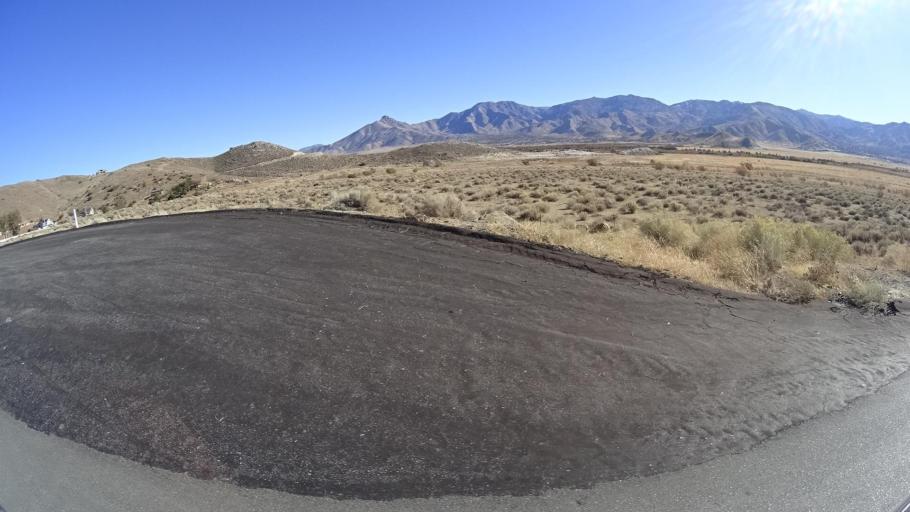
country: US
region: California
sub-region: Kern County
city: Wofford Heights
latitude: 35.6781
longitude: -118.3972
